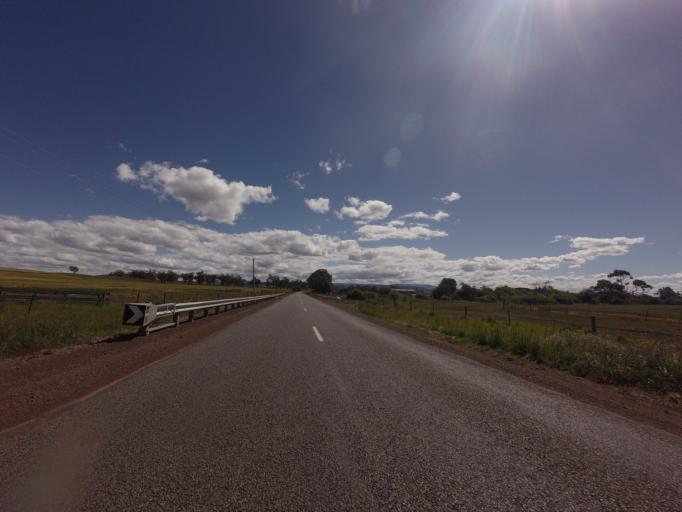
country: AU
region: Tasmania
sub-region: Northern Midlands
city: Evandale
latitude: -41.9413
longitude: 147.5404
